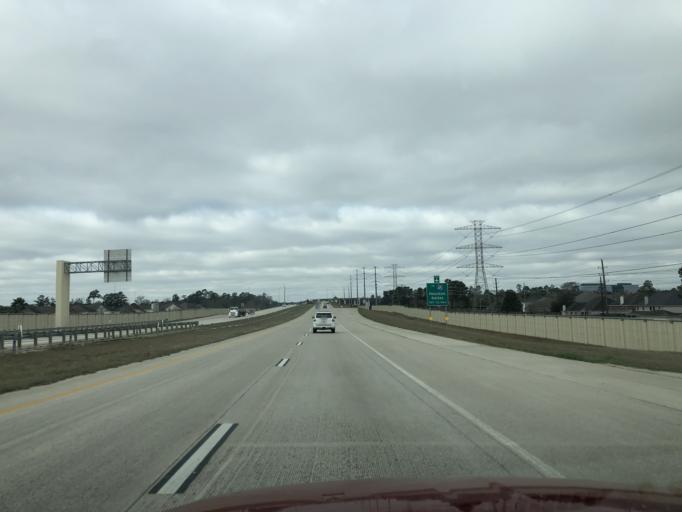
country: US
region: Texas
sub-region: Harris County
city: Spring
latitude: 30.0927
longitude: -95.4226
